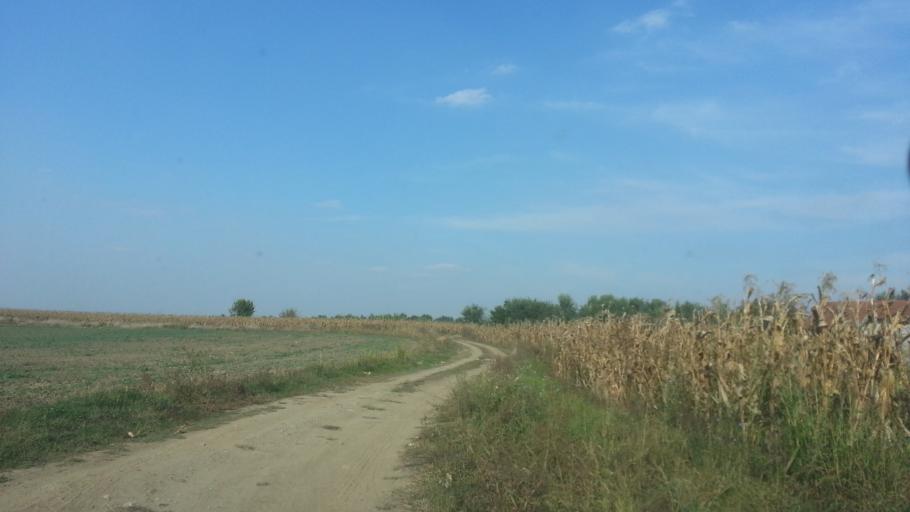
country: RS
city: Stari Banovci
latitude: 44.9893
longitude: 20.2726
